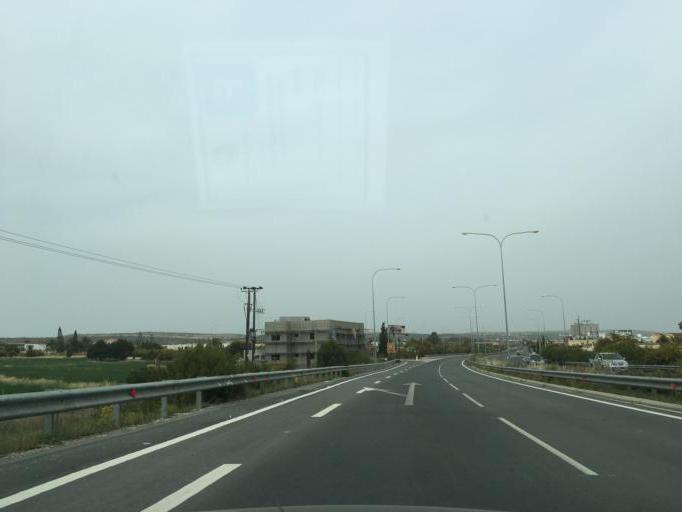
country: CY
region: Ammochostos
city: Ayia Napa
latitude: 34.9902
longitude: 33.9479
